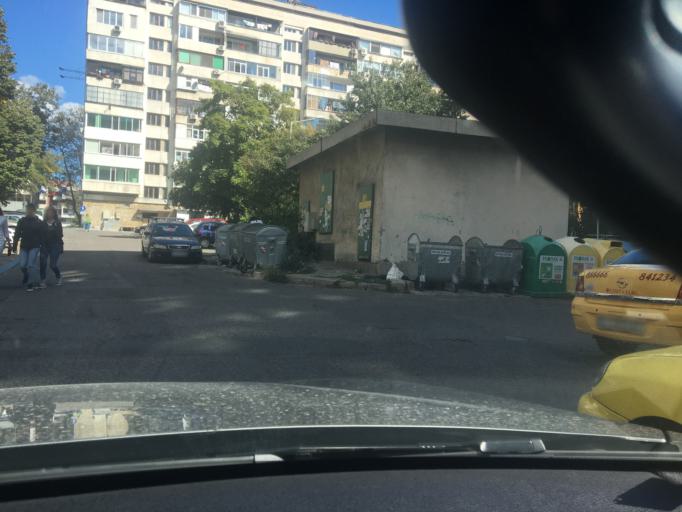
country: BG
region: Burgas
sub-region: Obshtina Burgas
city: Burgas
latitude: 42.5030
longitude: 27.4738
